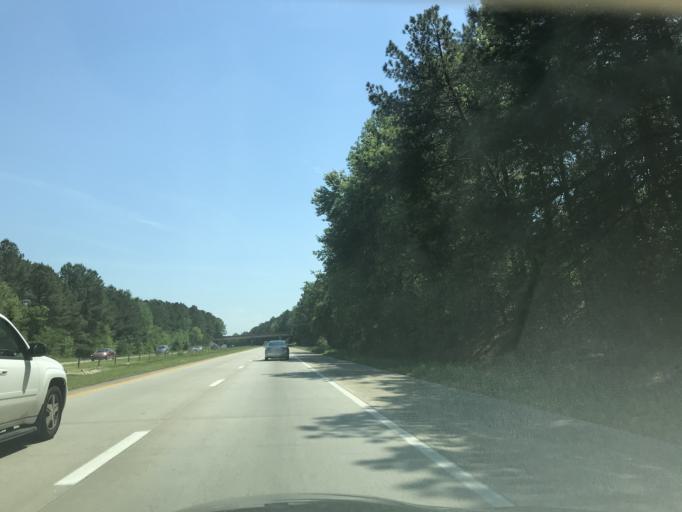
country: US
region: North Carolina
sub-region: Johnston County
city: Benson
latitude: 35.4756
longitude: -78.5500
